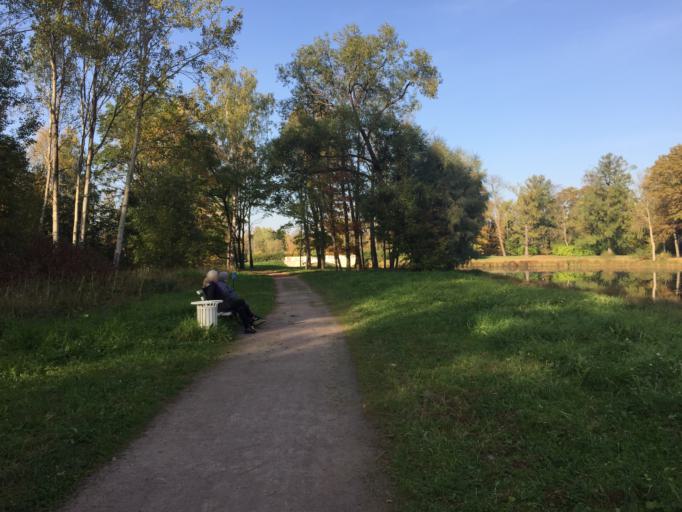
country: RU
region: St.-Petersburg
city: Pushkin
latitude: 59.7209
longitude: 30.3717
